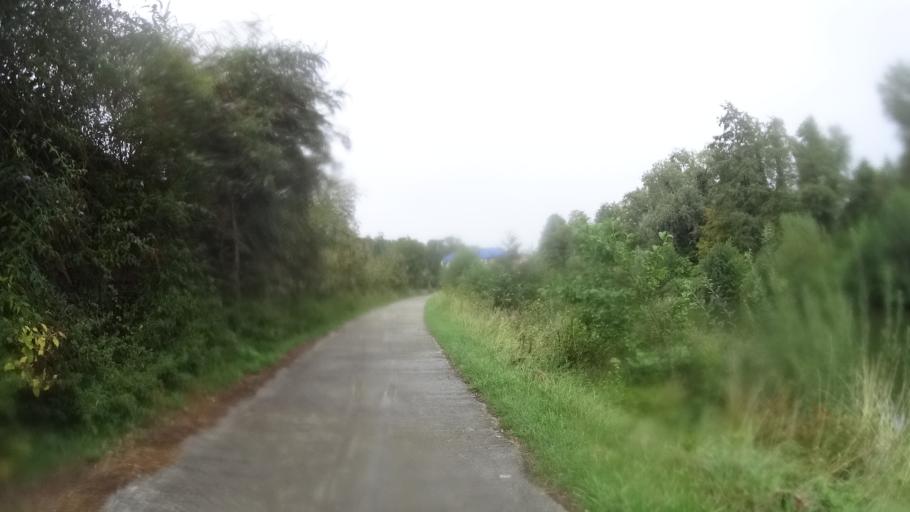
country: FR
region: Nord-Pas-de-Calais
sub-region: Departement du Nord
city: Louvroil
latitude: 50.2722
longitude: 3.9582
